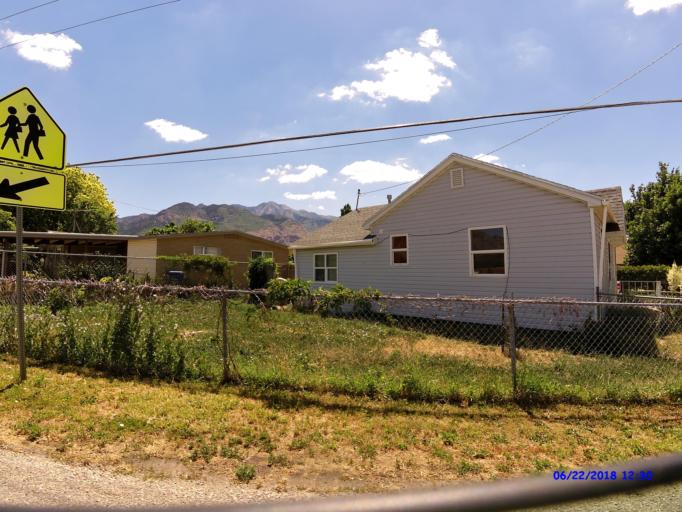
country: US
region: Utah
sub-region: Weber County
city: Ogden
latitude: 41.2405
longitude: -111.9575
